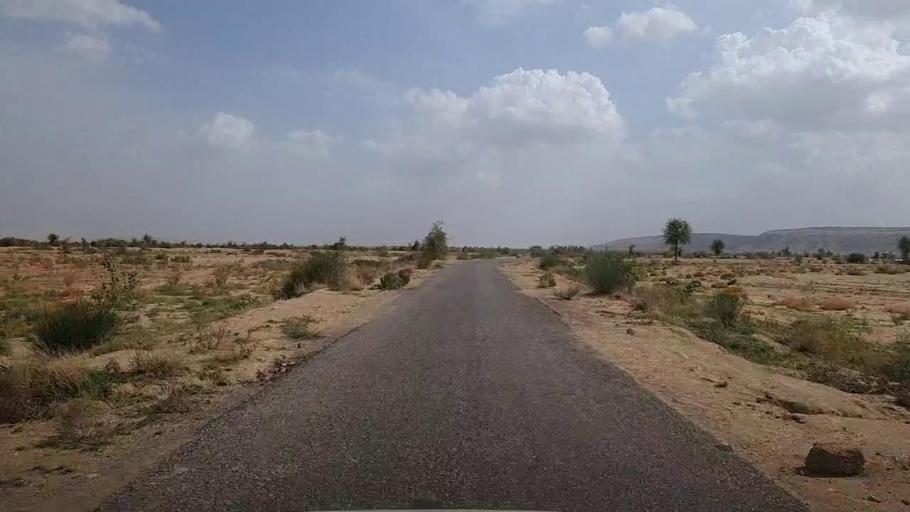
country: PK
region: Sindh
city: Jamshoro
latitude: 25.3987
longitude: 67.7661
